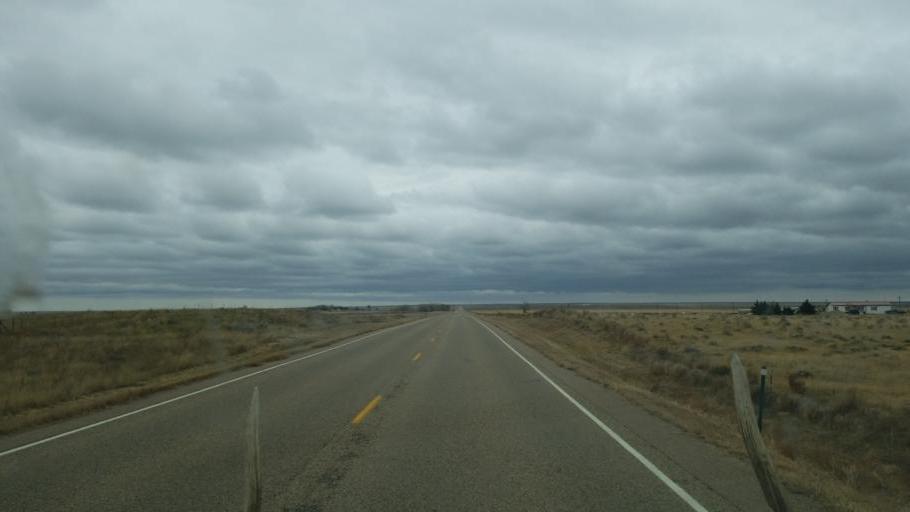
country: US
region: Colorado
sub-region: Kiowa County
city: Eads
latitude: 38.7804
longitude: -102.7201
